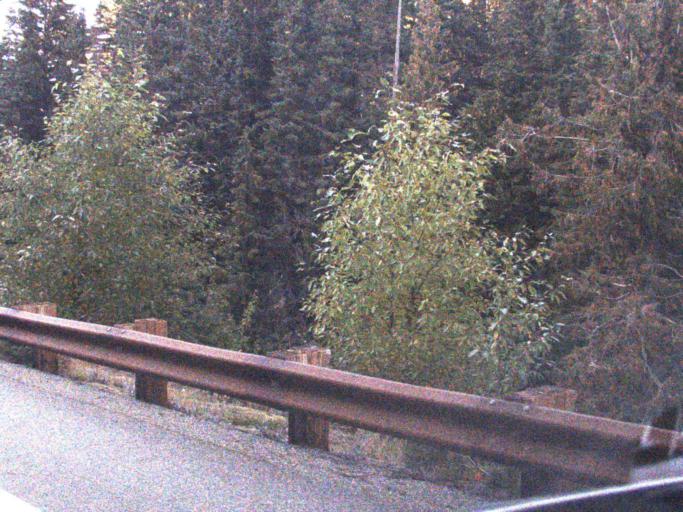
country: US
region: Washington
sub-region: Snohomish County
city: Darrington
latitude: 48.6288
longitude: -120.8433
